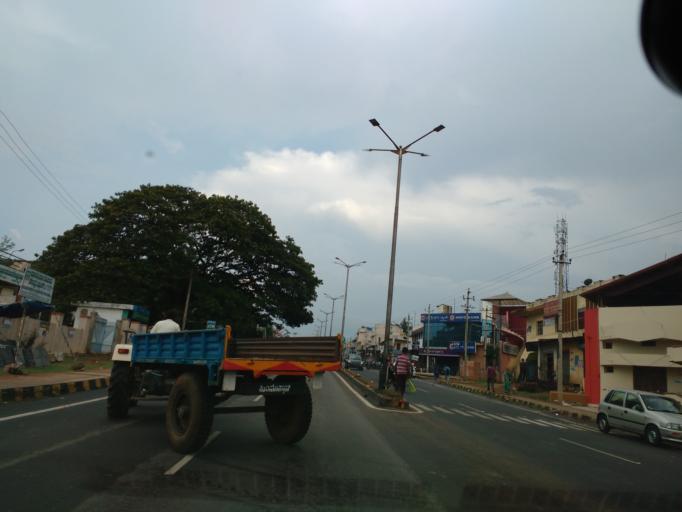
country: IN
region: Karnataka
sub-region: Hassan
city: Arsikere
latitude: 13.3204
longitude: 76.2517
